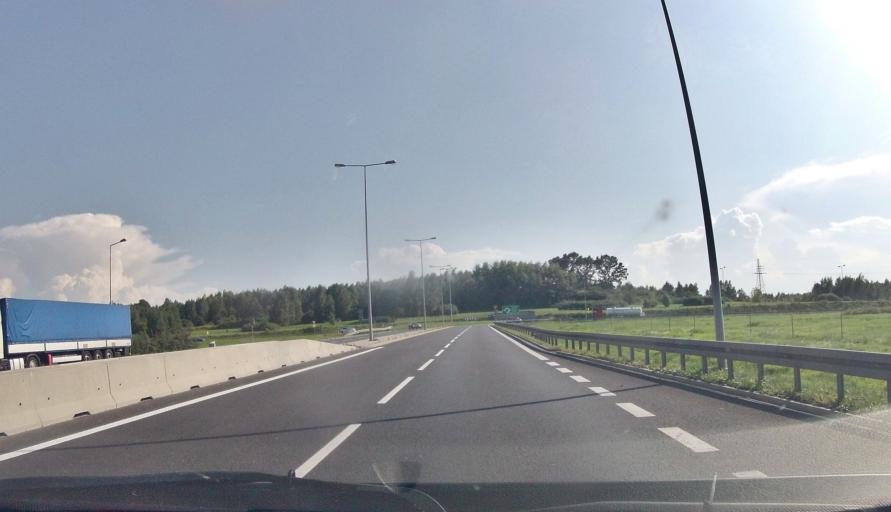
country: PL
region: Lesser Poland Voivodeship
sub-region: Powiat tarnowski
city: Lisia Gora
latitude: 50.0500
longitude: 21.0145
